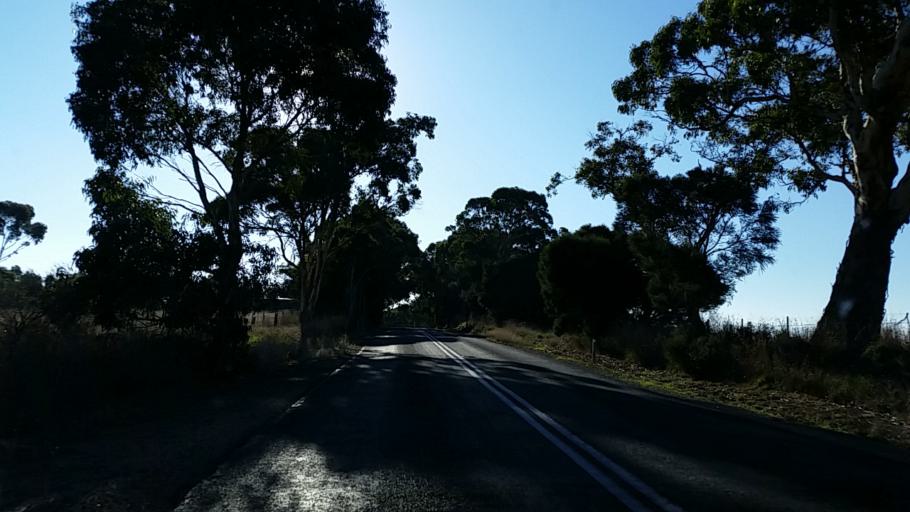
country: AU
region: South Australia
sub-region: Mount Barker
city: Mount Barker
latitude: -35.1160
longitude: 138.8936
